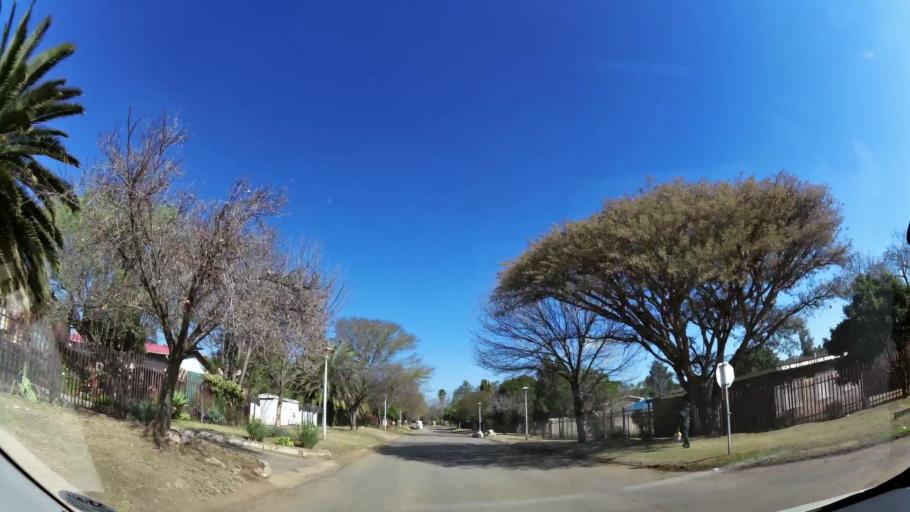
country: ZA
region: Mpumalanga
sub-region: Nkangala District Municipality
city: Witbank
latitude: -25.8483
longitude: 29.2475
